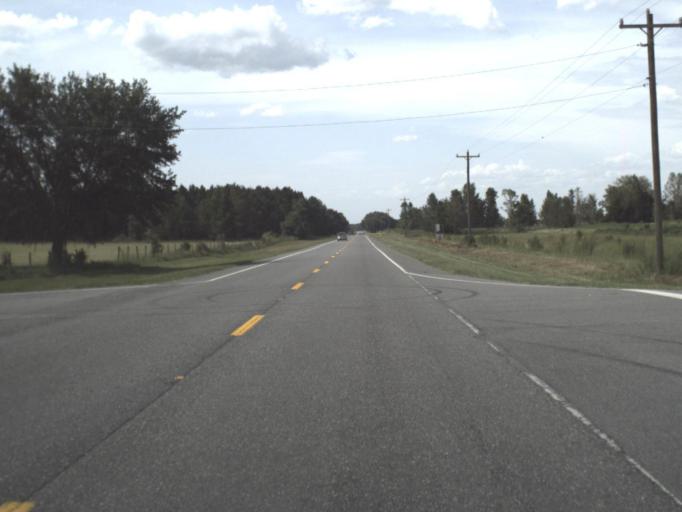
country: US
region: Florida
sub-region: Columbia County
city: Lake City
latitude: 30.0067
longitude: -82.7101
